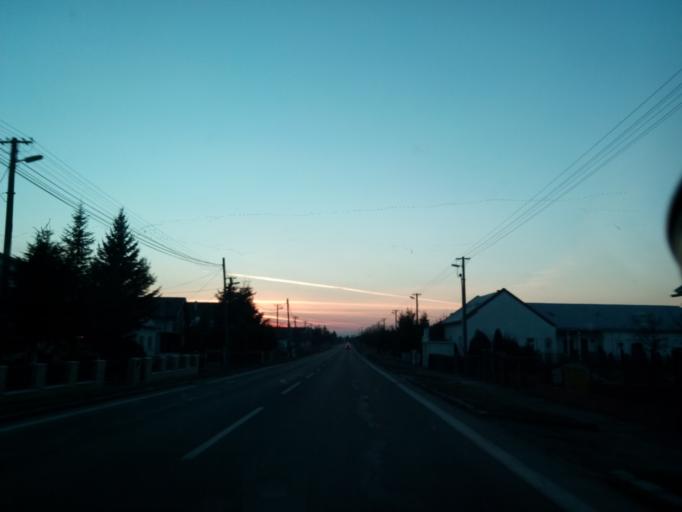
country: SK
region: Kosicky
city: Vinne
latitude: 48.7670
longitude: 22.0395
